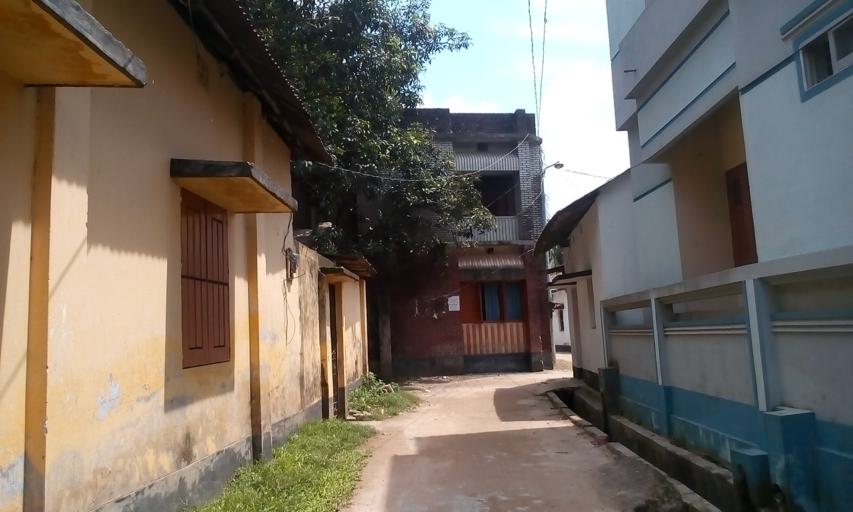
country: IN
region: West Bengal
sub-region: Dakshin Dinajpur
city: Balurghat
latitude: 25.3901
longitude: 88.9885
